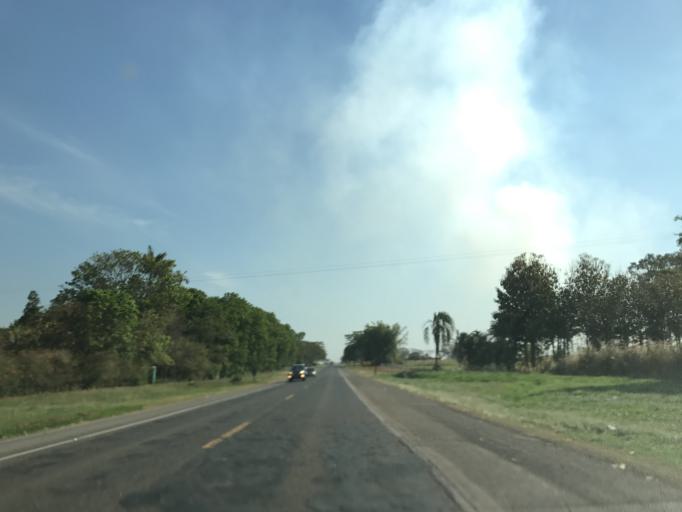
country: BR
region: Sao Paulo
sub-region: Penapolis
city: Penapolis
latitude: -21.3905
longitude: -50.1005
